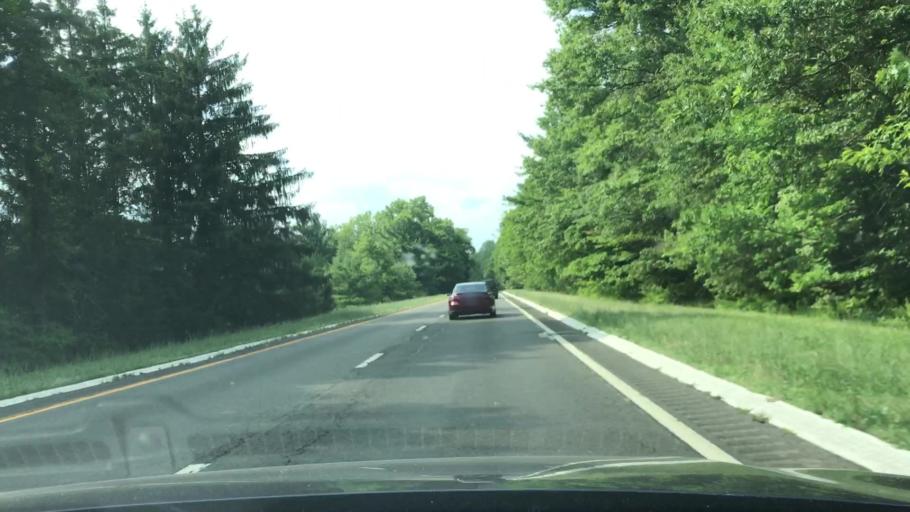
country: US
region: New York
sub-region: Rockland County
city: Bardonia
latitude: 41.1130
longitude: -74.0017
